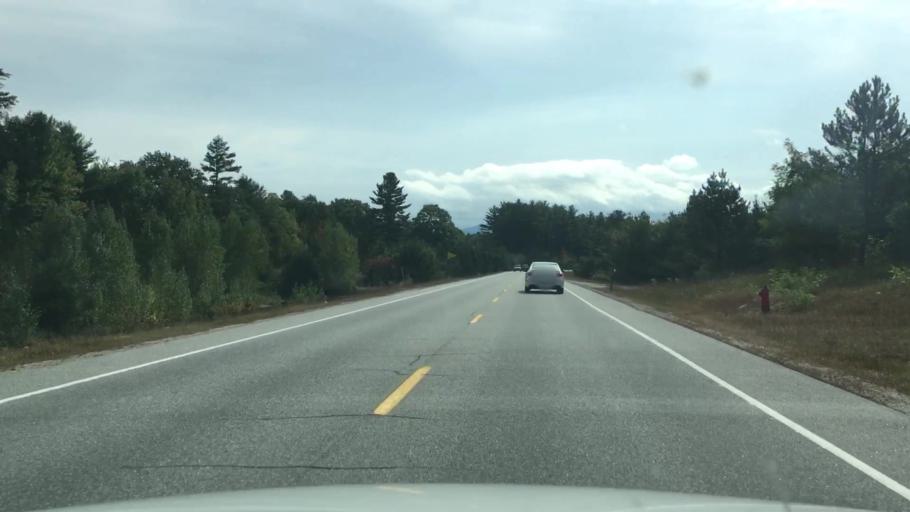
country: US
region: New Hampshire
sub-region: Carroll County
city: North Conway
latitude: 44.0262
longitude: -71.1105
